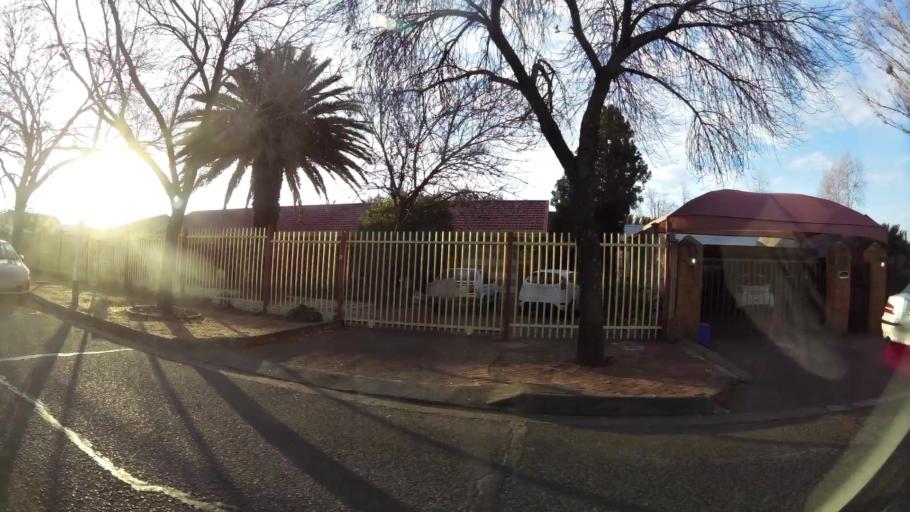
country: ZA
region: Orange Free State
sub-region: Mangaung Metropolitan Municipality
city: Bloemfontein
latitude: -29.1392
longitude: 26.1870
